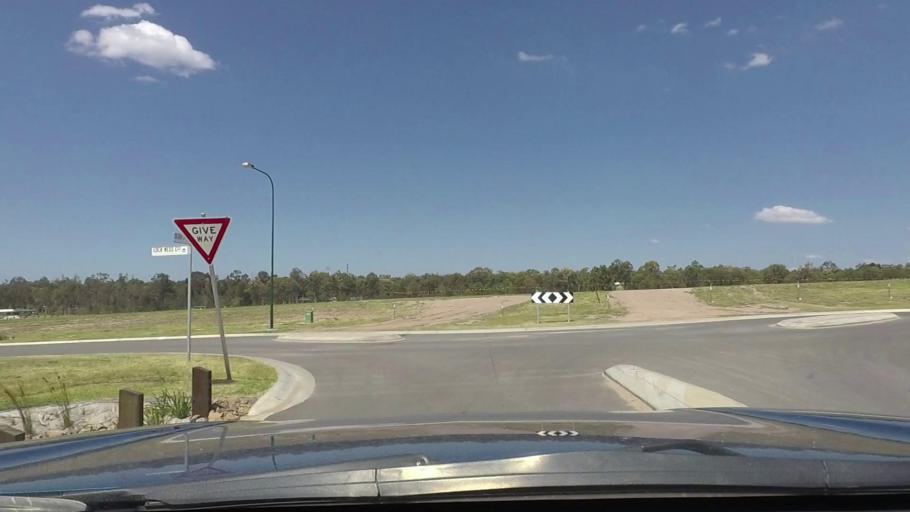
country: AU
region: Queensland
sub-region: Logan
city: North Maclean
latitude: -27.7389
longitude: 152.9506
